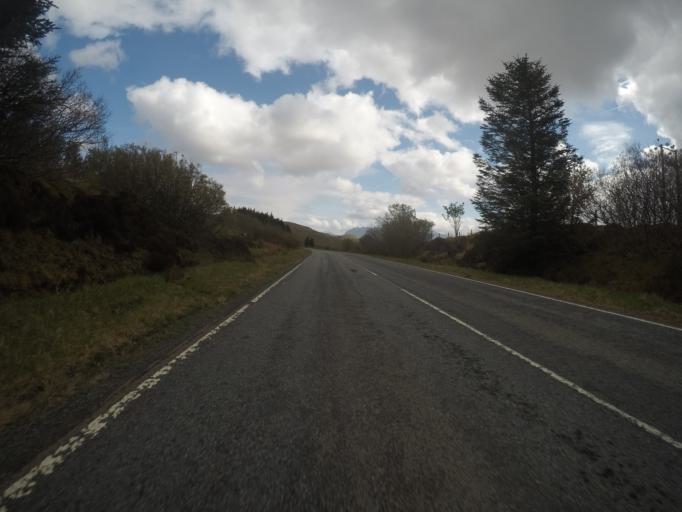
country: GB
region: Scotland
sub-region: Highland
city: Isle of Skye
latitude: 57.3330
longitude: -6.3475
